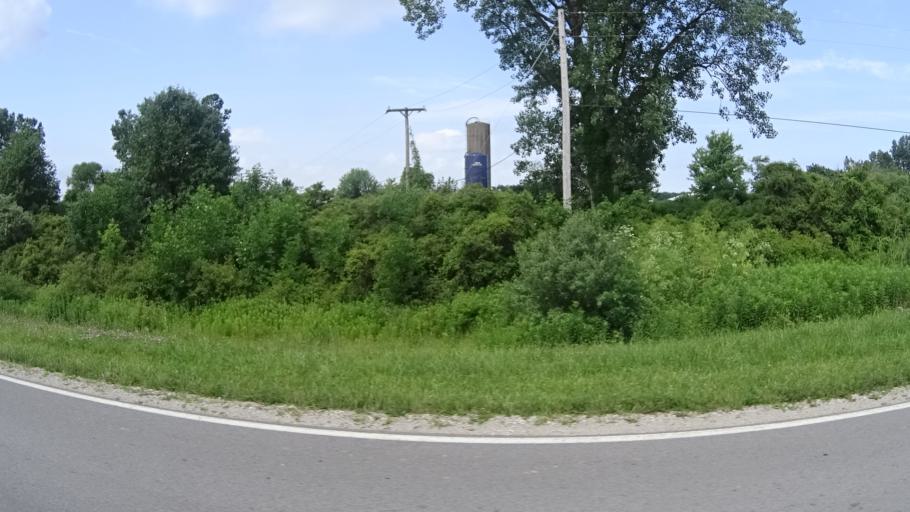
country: US
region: Ohio
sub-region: Lorain County
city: Vermilion
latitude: 41.3917
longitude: -82.4061
